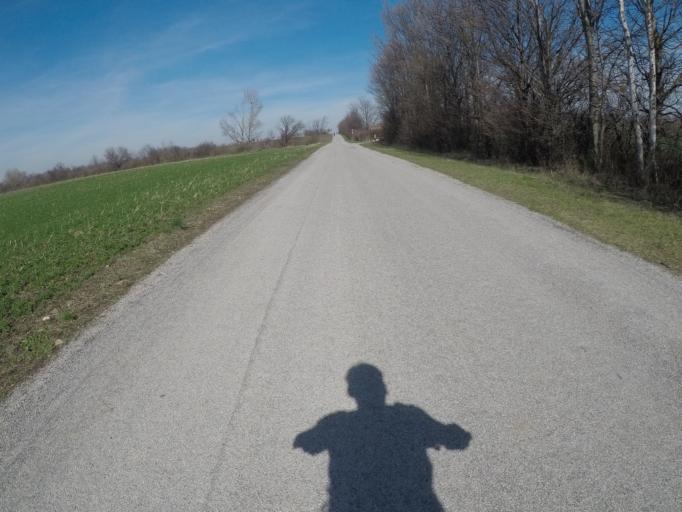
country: AT
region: Lower Austria
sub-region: Politischer Bezirk Modling
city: Biedermannsdorf
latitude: 48.0971
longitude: 16.3399
